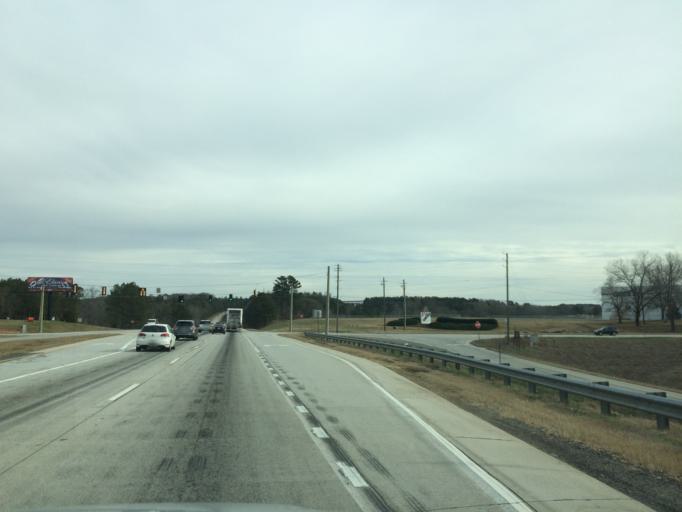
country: US
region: Georgia
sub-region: Barrow County
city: Auburn
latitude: 33.9678
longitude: -83.8210
